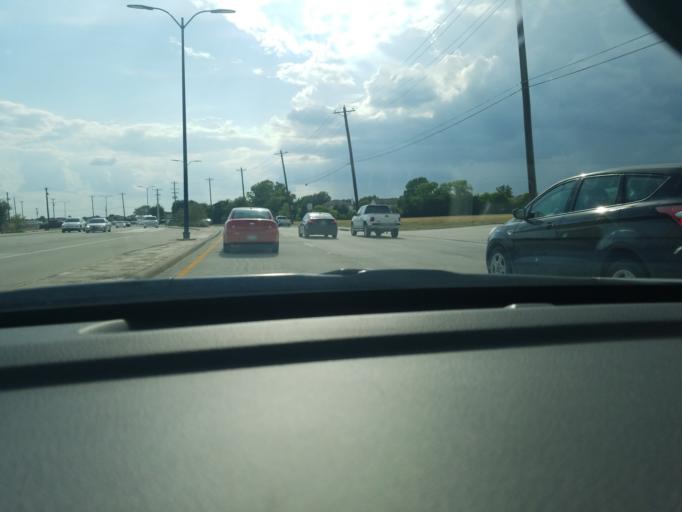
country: US
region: Texas
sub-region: Denton County
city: Little Elm
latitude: 33.1690
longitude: -96.9231
